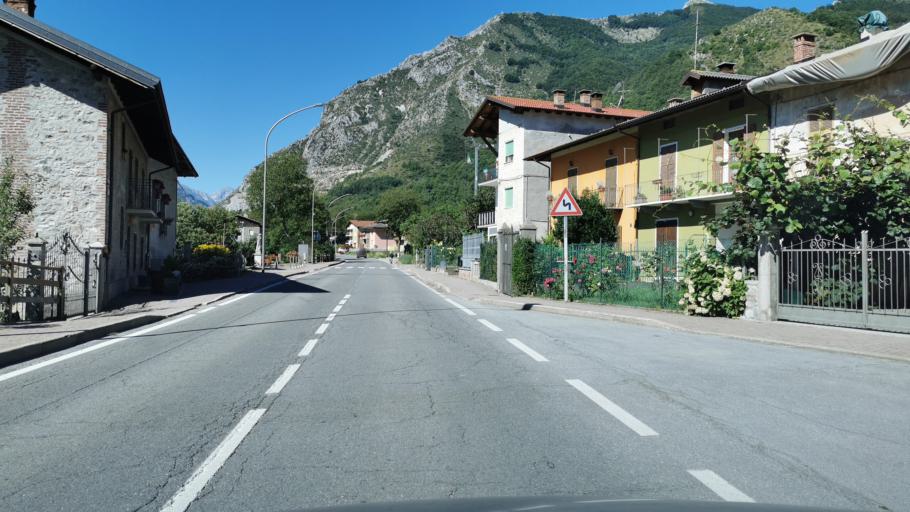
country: IT
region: Piedmont
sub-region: Provincia di Cuneo
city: Roaschia
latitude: 44.2931
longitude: 7.4292
